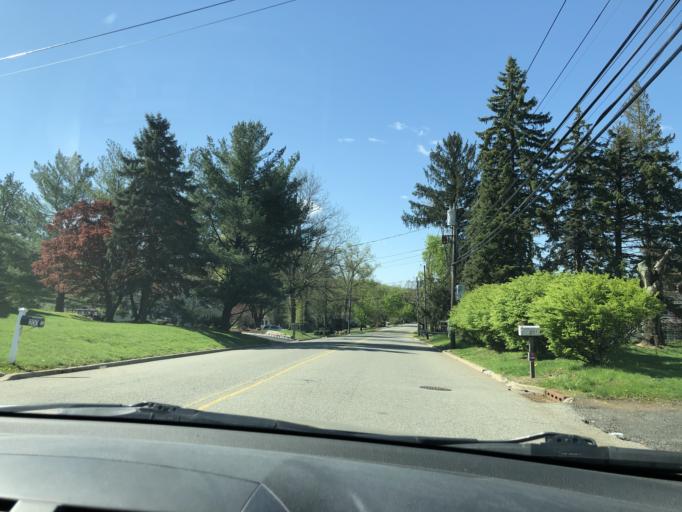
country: US
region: New Jersey
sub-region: Essex County
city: North Caldwell
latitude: 40.8489
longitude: -74.2595
